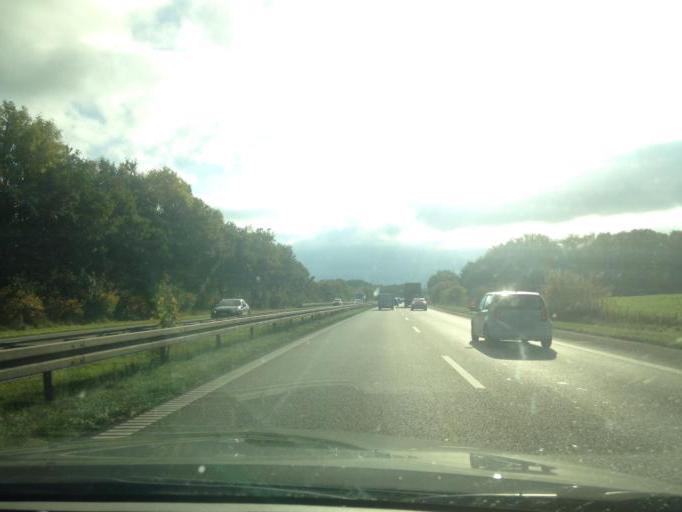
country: DK
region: South Denmark
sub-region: Fredericia Kommune
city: Taulov
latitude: 55.5921
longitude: 9.5842
